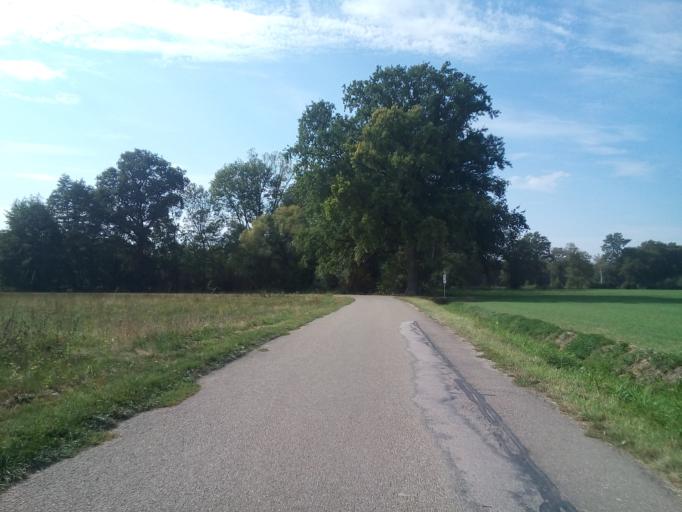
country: DE
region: Baden-Wuerttemberg
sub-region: Karlsruhe Region
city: Zell
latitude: 48.6684
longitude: 8.0818
